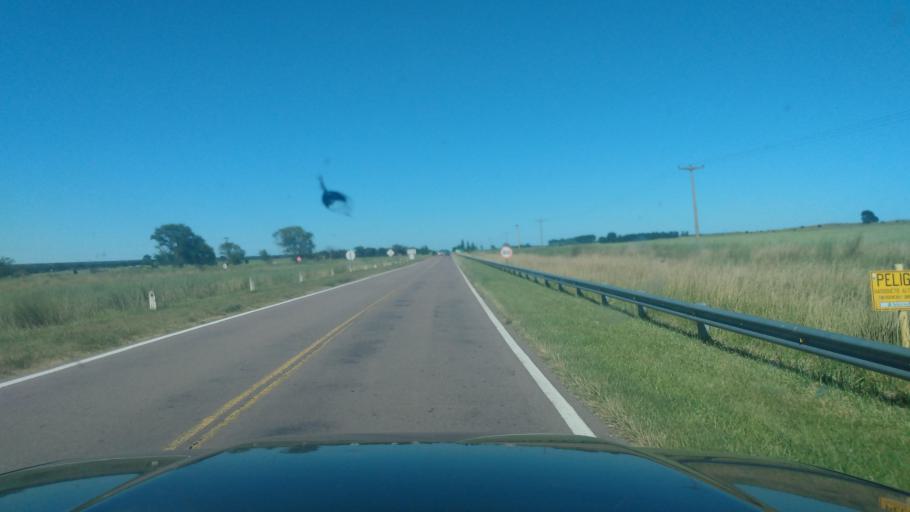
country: AR
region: La Pampa
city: General Acha
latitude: -37.3129
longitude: -64.2923
